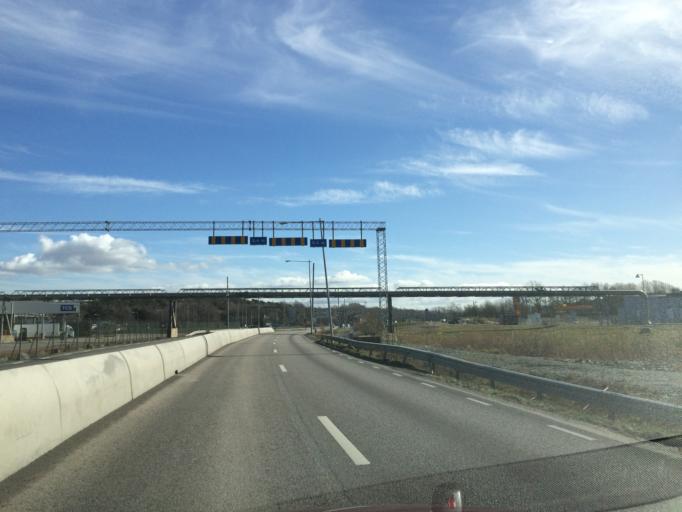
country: SE
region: Vaestra Goetaland
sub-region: Goteborg
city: Torslanda
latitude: 57.7144
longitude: 11.8362
